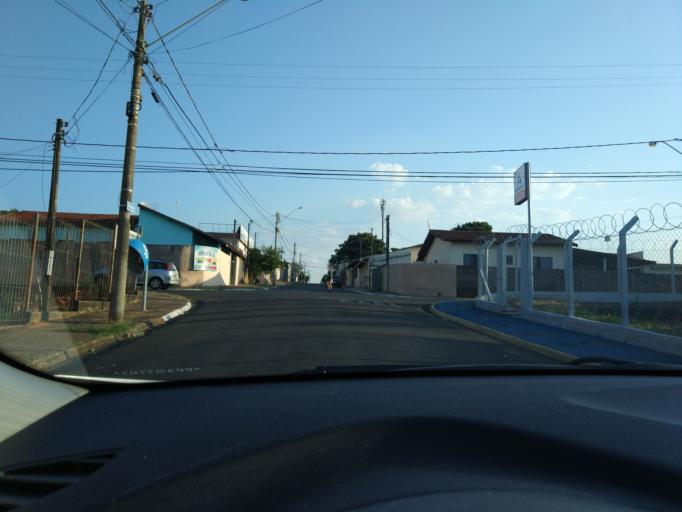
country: BR
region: Sao Paulo
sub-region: Botucatu
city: Botucatu
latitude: -22.8981
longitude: -48.4348
